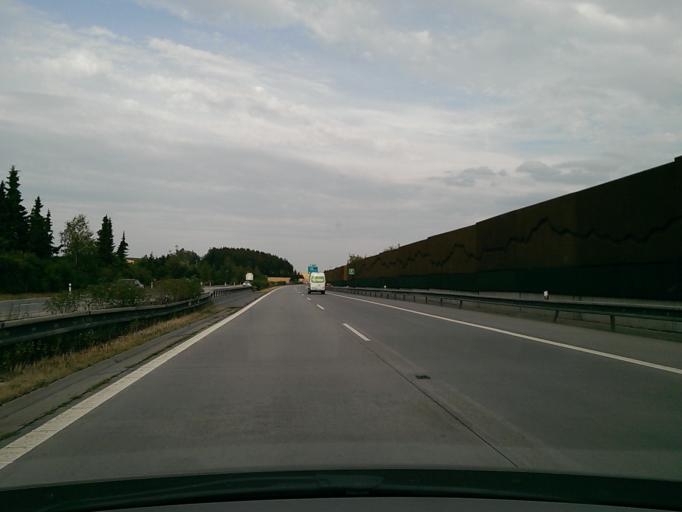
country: CZ
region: Vysocina
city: Merin
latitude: 49.3979
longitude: 15.8770
